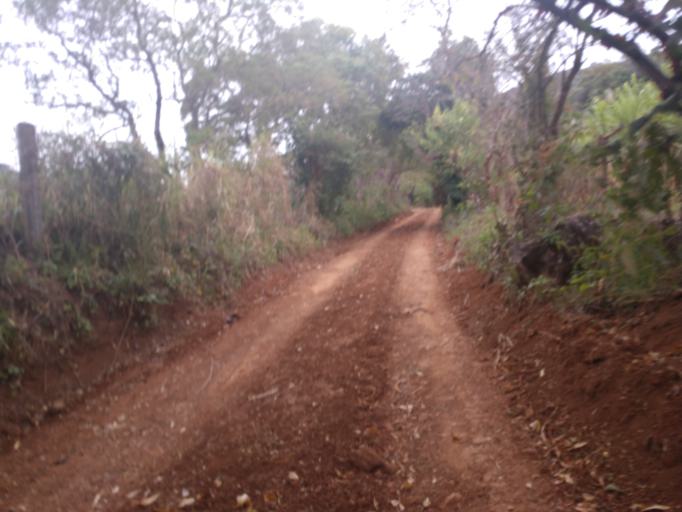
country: MX
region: Nayarit
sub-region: Tepic
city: La Corregidora
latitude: 21.4693
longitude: -104.7892
